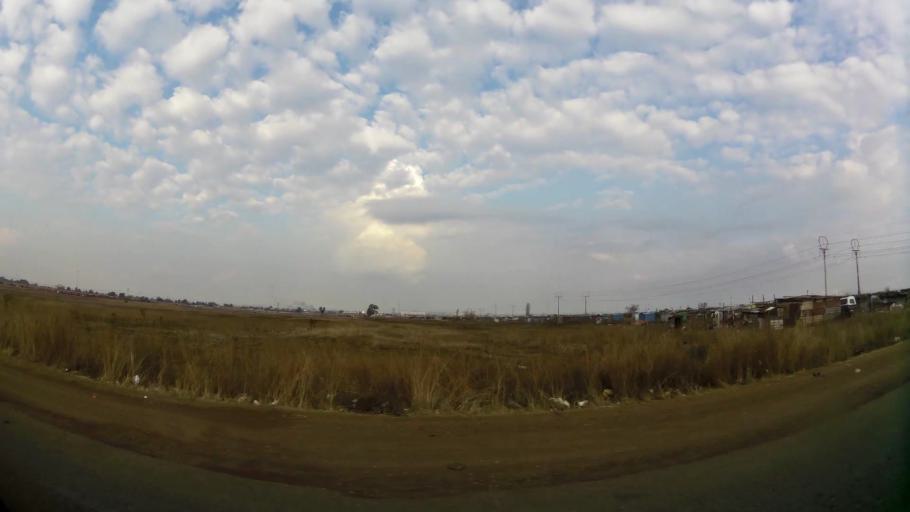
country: ZA
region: Gauteng
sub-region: Sedibeng District Municipality
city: Vanderbijlpark
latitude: -26.6604
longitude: 27.8669
